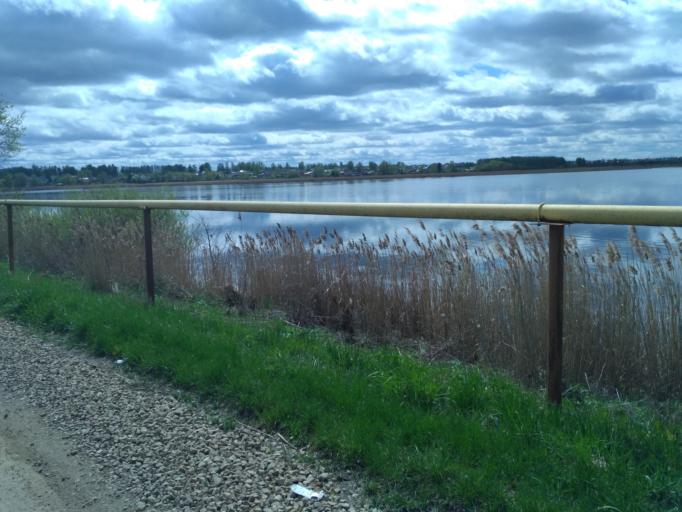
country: RU
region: Nizjnij Novgorod
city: Vad
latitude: 55.5413
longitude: 44.2011
